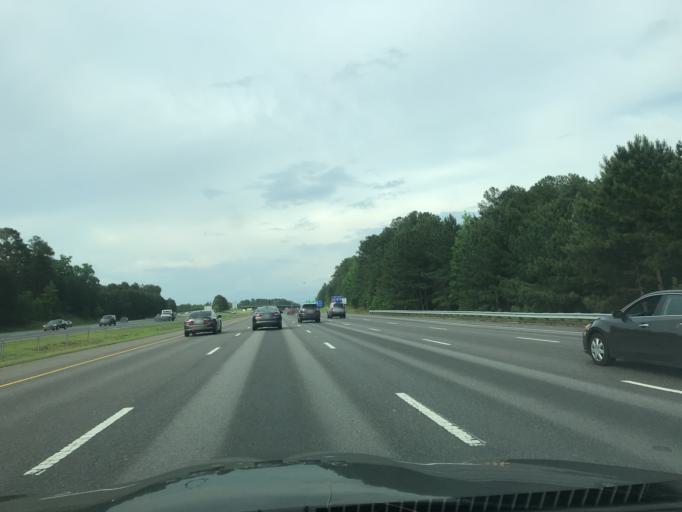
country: US
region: North Carolina
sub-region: Wake County
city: Morrisville
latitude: 35.9008
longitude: -78.7803
